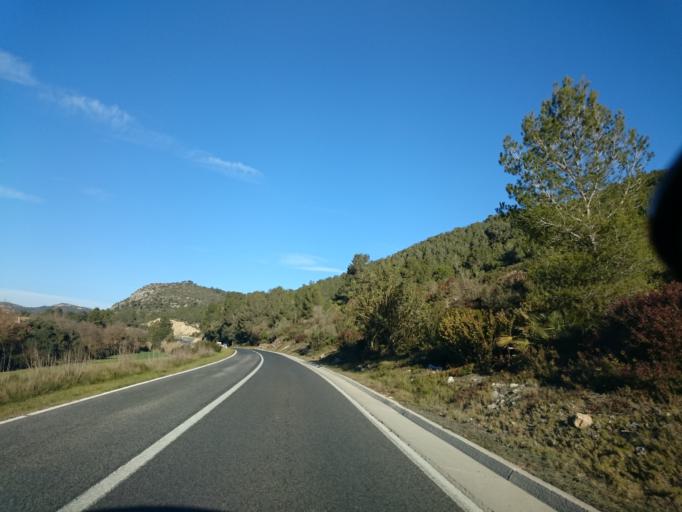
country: ES
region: Catalonia
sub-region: Provincia de Barcelona
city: Sant Pere de Ribes
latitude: 41.2837
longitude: 1.7502
